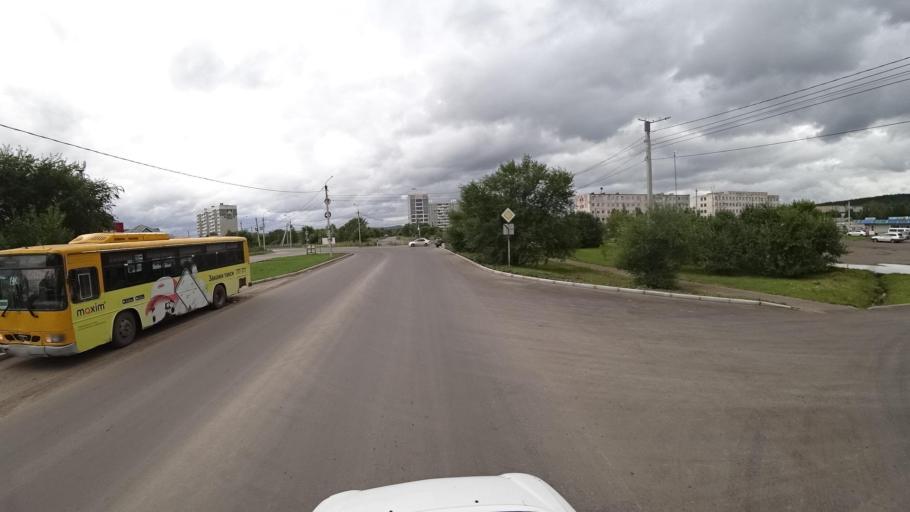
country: RU
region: Khabarovsk Krai
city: Solnechnyy
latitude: 50.5942
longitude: 137.0388
